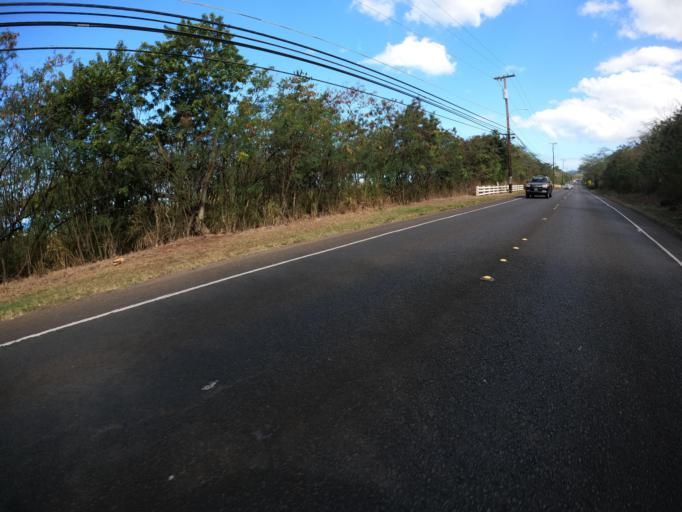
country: US
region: Hawaii
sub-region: Honolulu County
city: Pupukea
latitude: 21.6343
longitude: -158.0693
